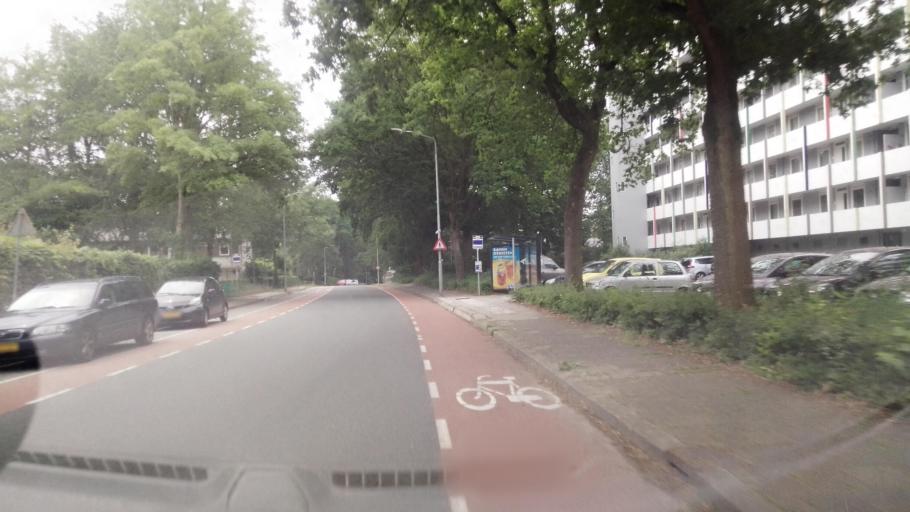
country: NL
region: Limburg
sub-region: Gemeente Venlo
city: Venlo
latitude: 51.3607
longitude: 6.1888
